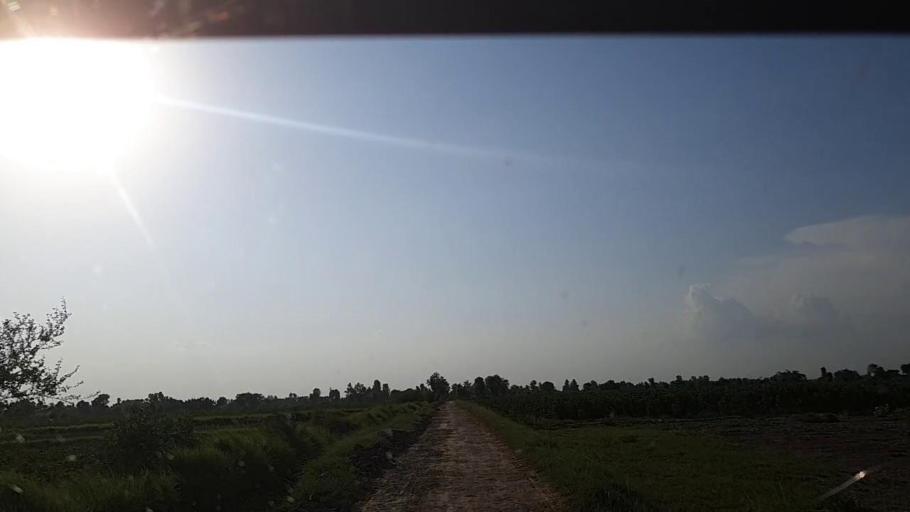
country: PK
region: Sindh
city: Pano Aqil
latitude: 27.9063
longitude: 69.2059
